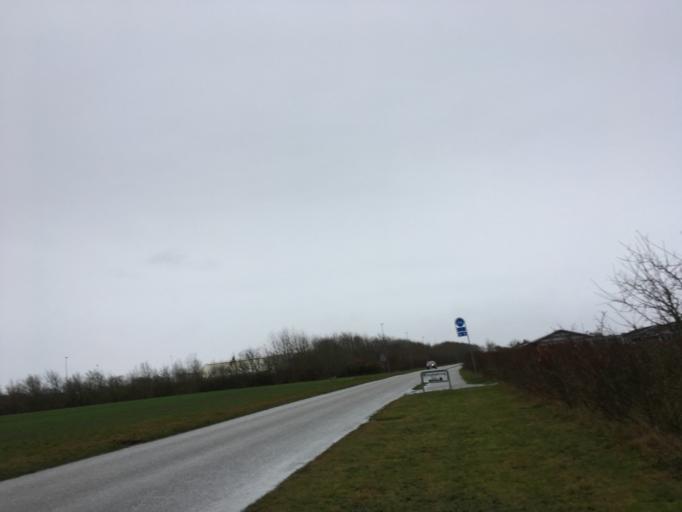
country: DK
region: Central Jutland
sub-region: Ringkobing-Skjern Kommune
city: Ringkobing
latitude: 56.0997
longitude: 8.2690
